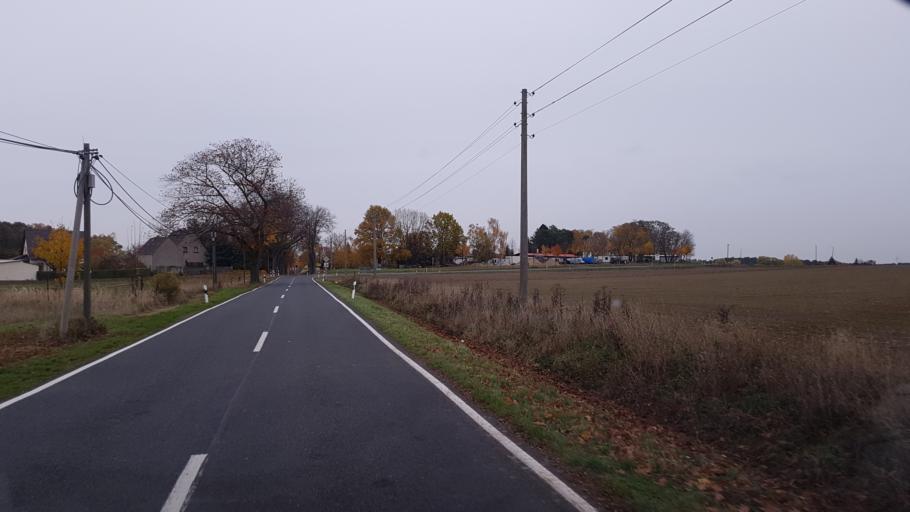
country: DE
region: Brandenburg
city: Crinitz
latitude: 51.7531
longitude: 13.8014
